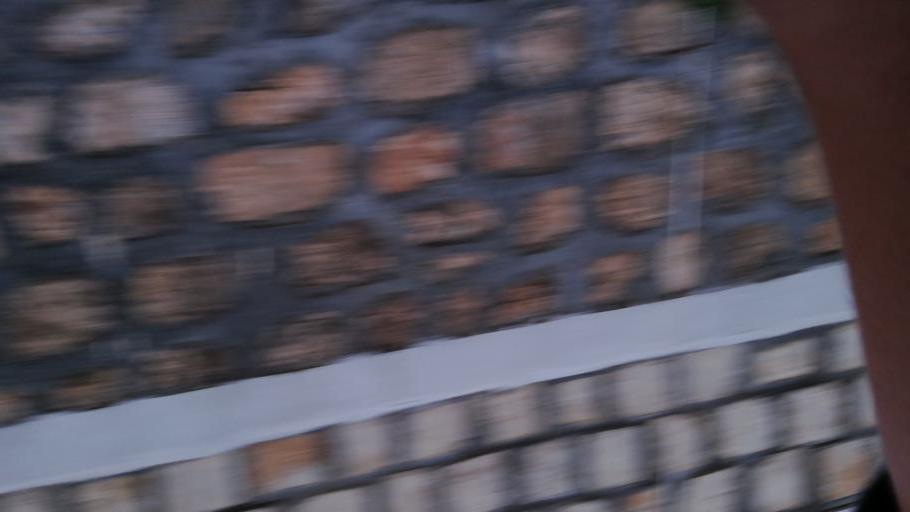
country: TR
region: Mardin
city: Kindirip
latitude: 37.4447
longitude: 41.2150
